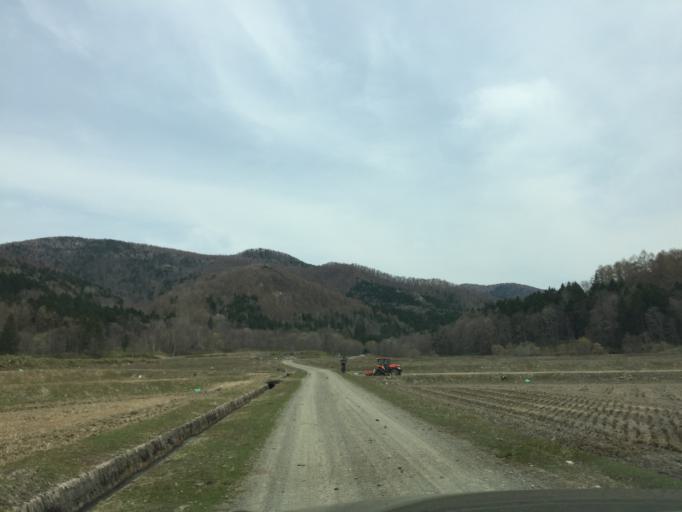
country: JP
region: Hokkaido
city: Ashibetsu
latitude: 43.6216
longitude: 142.2234
